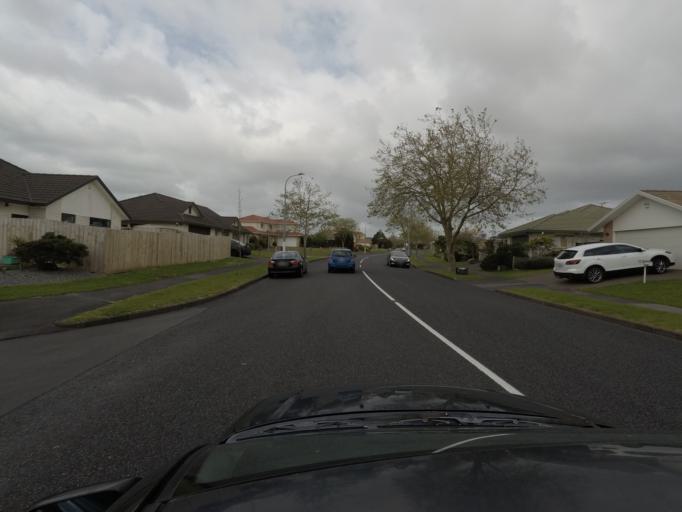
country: NZ
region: Auckland
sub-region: Auckland
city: Pakuranga
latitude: -36.9261
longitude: 174.9143
